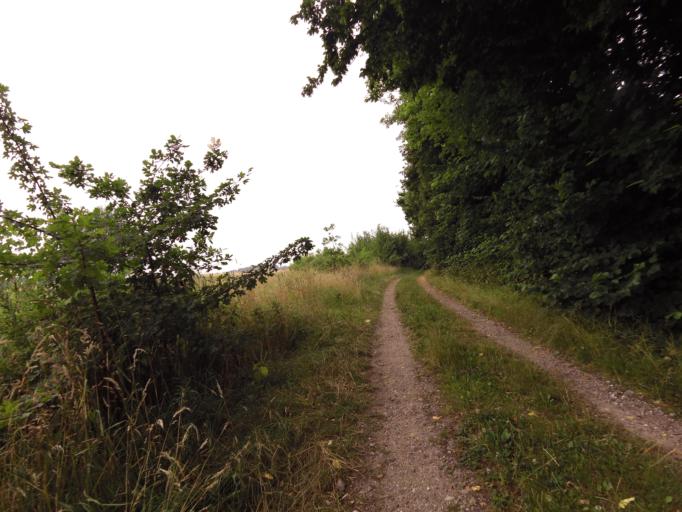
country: NL
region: Limburg
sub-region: Gemeente Voerendaal
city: Voerendaal
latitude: 50.8877
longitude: 5.9518
